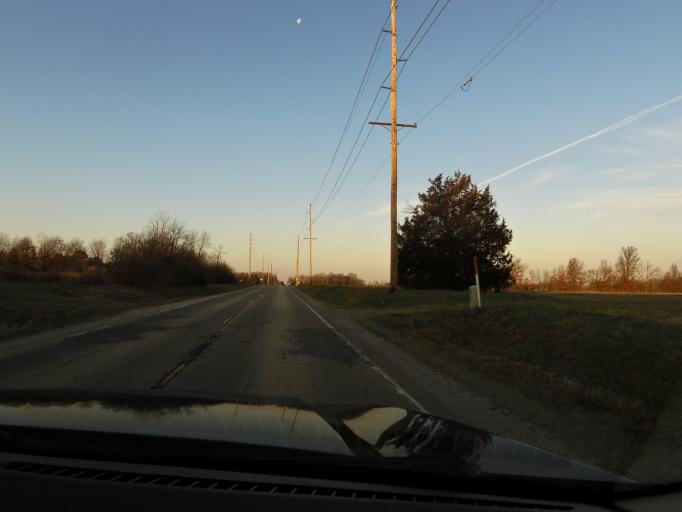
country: US
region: Illinois
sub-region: Marion County
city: Odin
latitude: 38.7650
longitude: -89.0796
